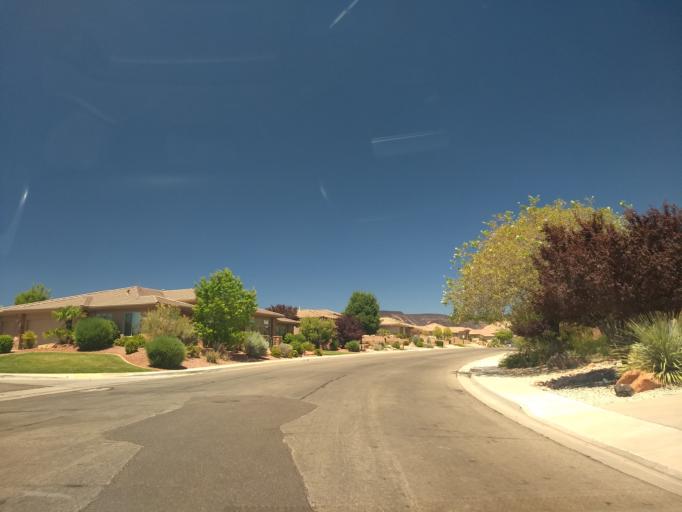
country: US
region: Utah
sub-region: Washington County
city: Washington
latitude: 37.1502
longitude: -113.5214
